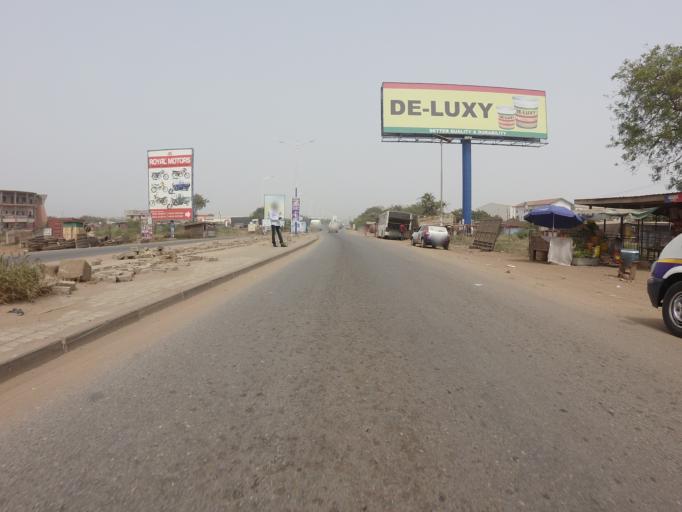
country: GH
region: Greater Accra
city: Tema
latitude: 5.7167
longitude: 0.0152
